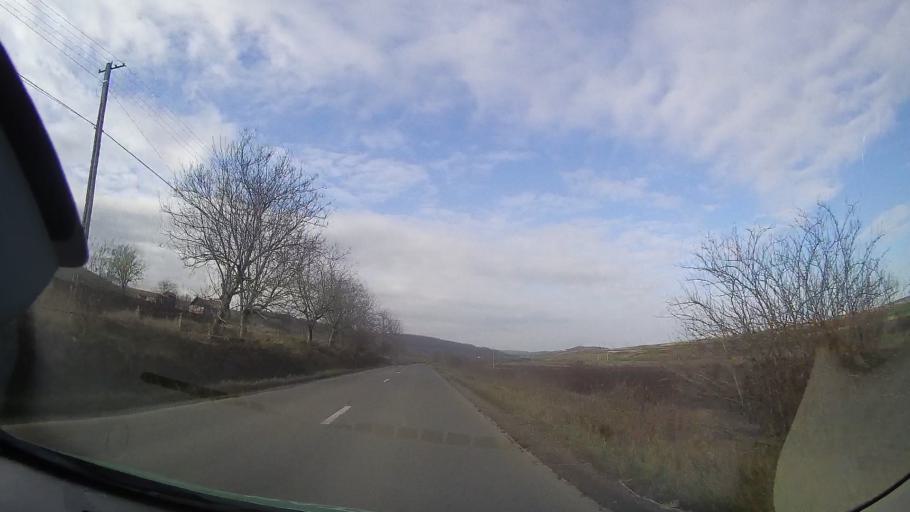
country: RO
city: Barza
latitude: 46.5496
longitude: 24.1190
